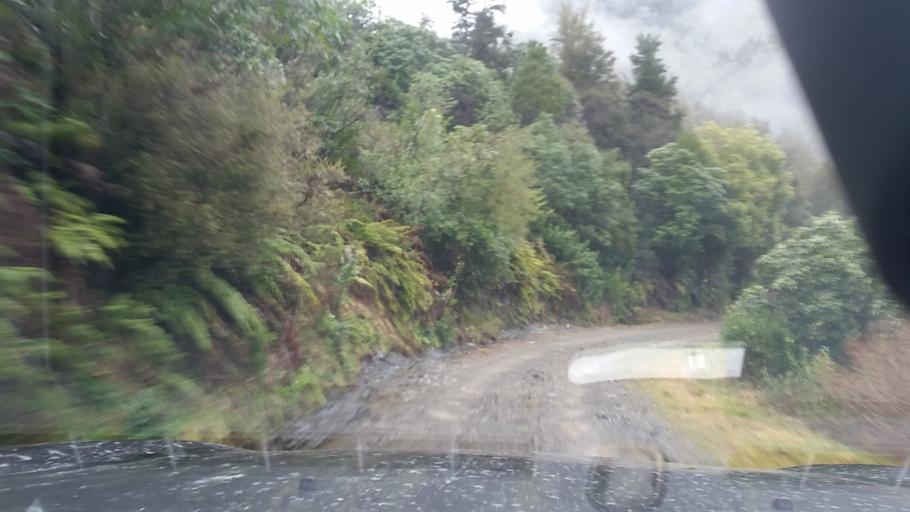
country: NZ
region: Nelson
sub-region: Nelson City
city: Nelson
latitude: -41.3757
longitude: 173.5946
